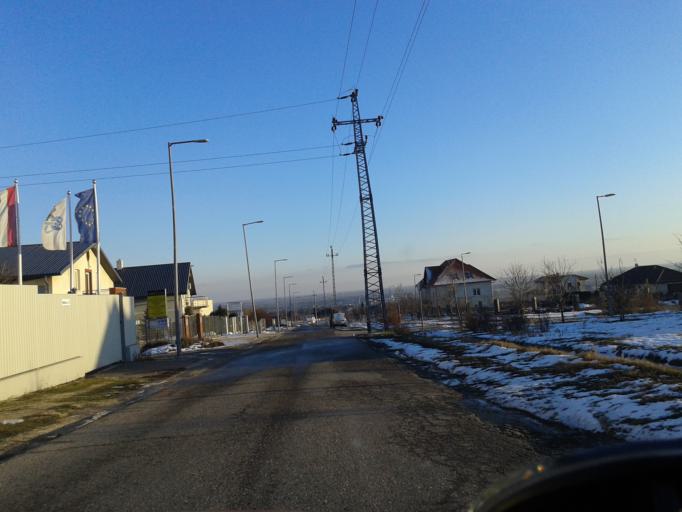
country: HU
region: Pest
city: Diosd
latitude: 47.4186
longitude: 18.9420
